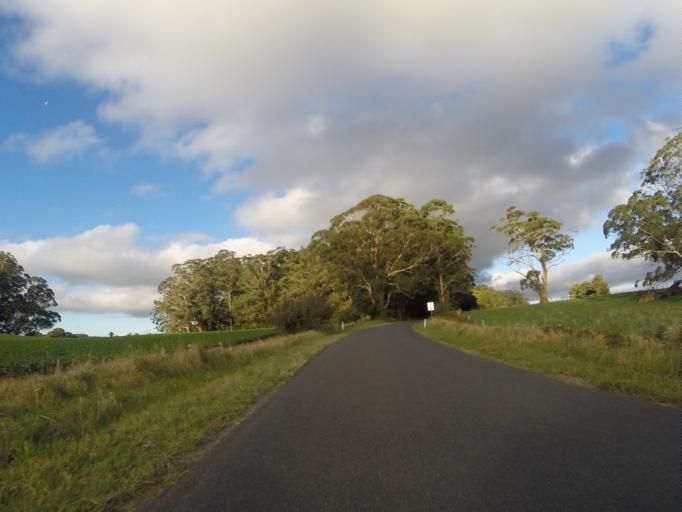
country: AU
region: New South Wales
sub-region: Shoalhaven Shire
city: Kangaroo Valley
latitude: -34.6073
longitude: 150.5384
